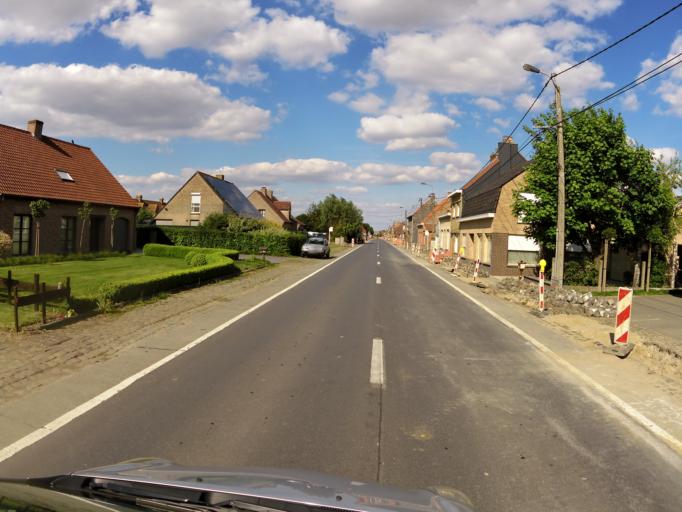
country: BE
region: Flanders
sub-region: Provincie West-Vlaanderen
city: Poperinge
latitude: 50.8931
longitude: 2.7759
